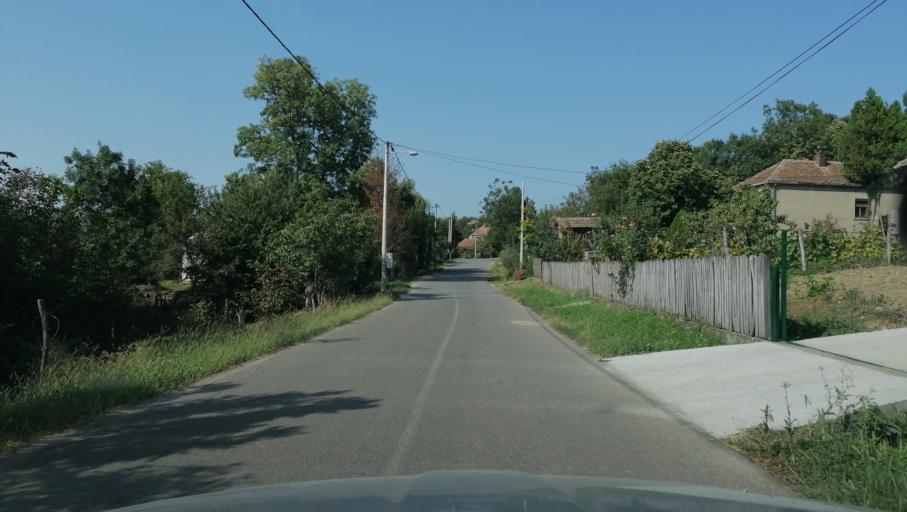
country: RS
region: Central Serbia
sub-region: Belgrade
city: Sopot
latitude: 44.5884
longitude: 20.6103
